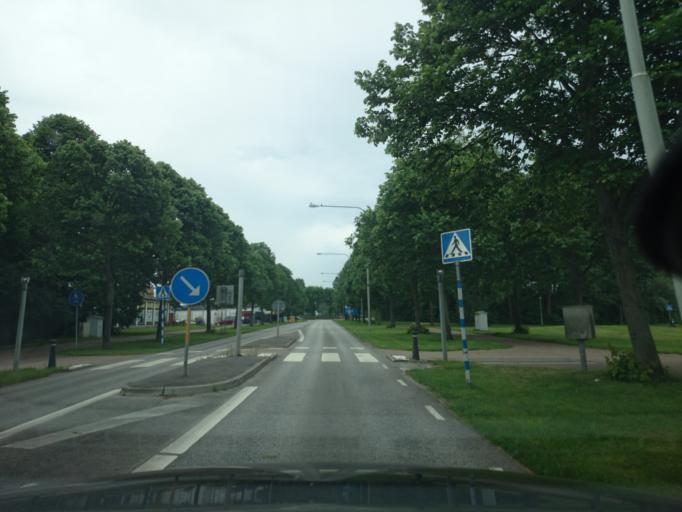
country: SE
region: Skane
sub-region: Landskrona
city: Landskrona
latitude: 55.8878
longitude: 12.8303
